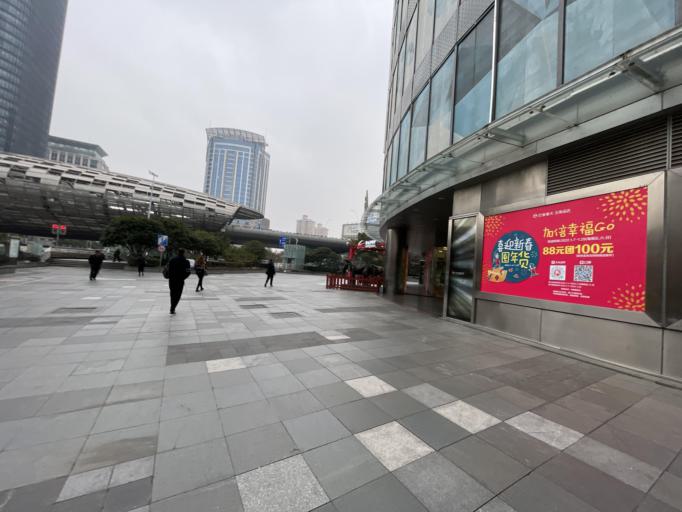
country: CN
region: Shanghai Shi
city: Yangpu
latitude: 31.3027
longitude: 121.5106
